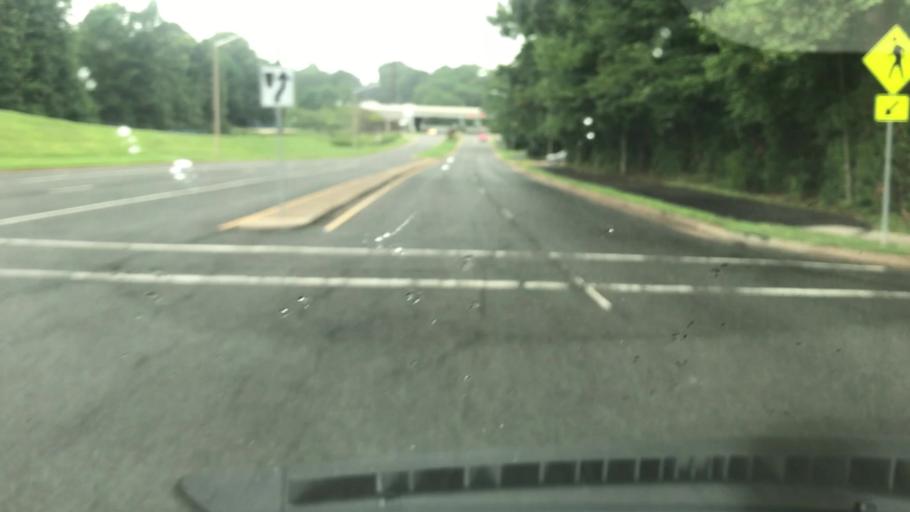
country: US
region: Virginia
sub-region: Fairfax County
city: Greenbriar
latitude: 38.8660
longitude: -77.3785
